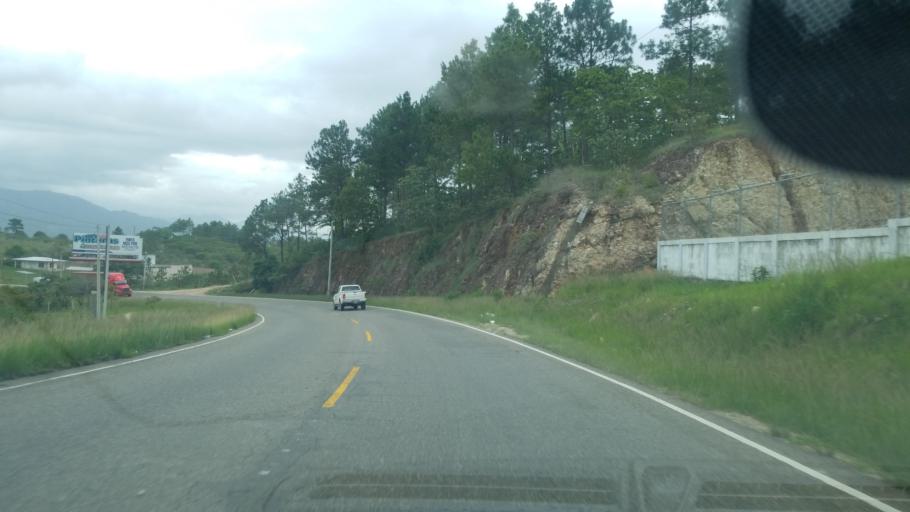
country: HN
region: Ocotepeque
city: Sinuapa
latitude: 14.4591
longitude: -89.1683
